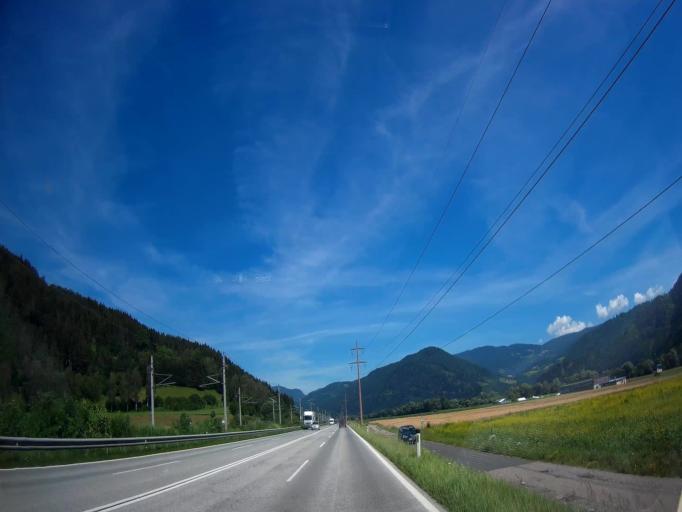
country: AT
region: Carinthia
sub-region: Politischer Bezirk Sankt Veit an der Glan
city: Micheldorf
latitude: 46.9245
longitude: 14.4291
